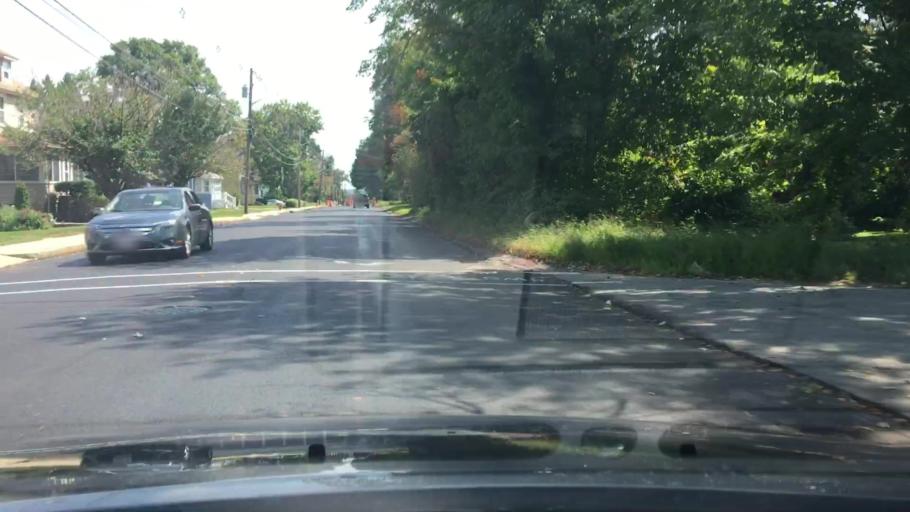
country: US
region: Massachusetts
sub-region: Worcester County
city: Milford
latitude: 42.1550
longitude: -71.5308
